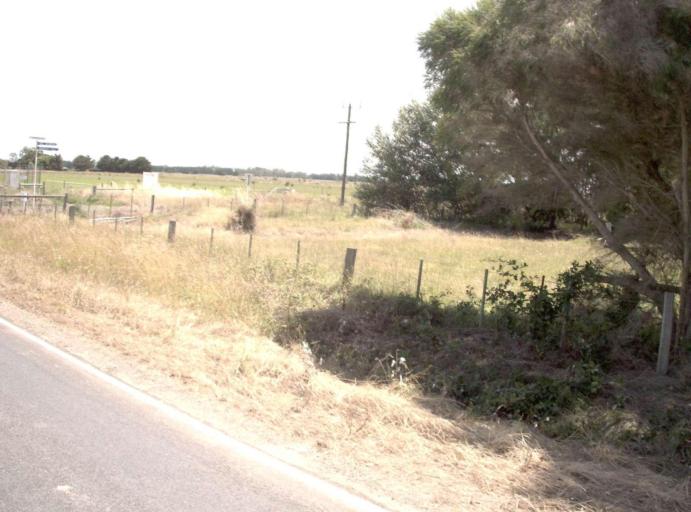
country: AU
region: Victoria
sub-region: Wellington
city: Heyfield
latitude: -38.0726
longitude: 146.8703
